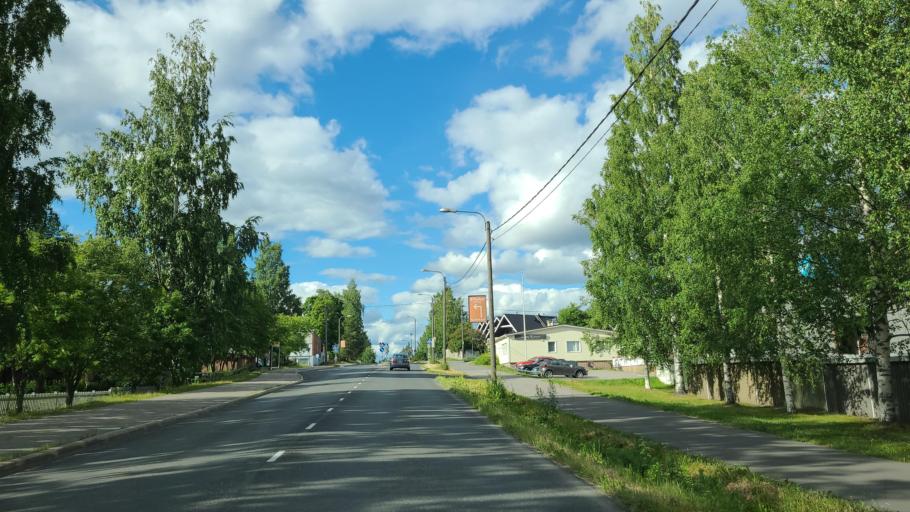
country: FI
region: Northern Savo
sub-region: Kuopio
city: Kuopio
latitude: 62.9245
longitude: 27.6321
